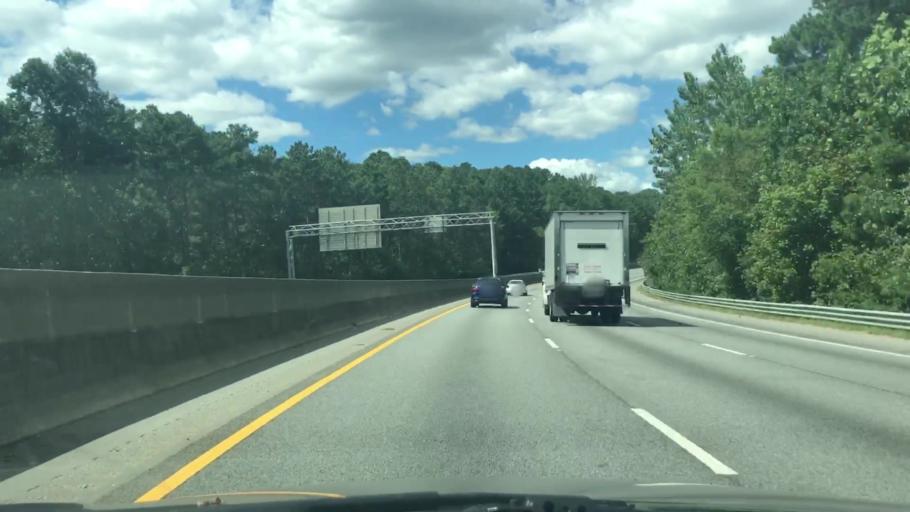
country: US
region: Georgia
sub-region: DeKalb County
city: Stone Mountain
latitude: 33.8215
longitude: -84.1705
